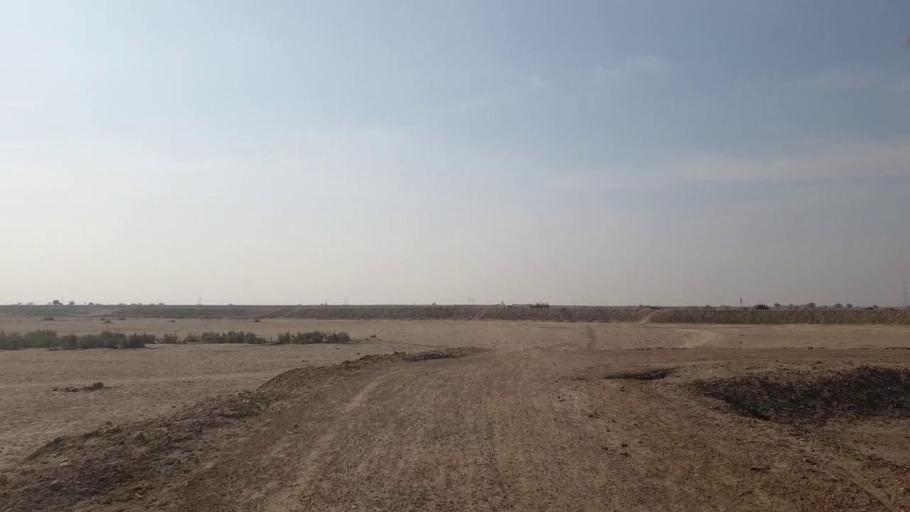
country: PK
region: Sindh
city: Sann
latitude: 25.9137
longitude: 68.2306
